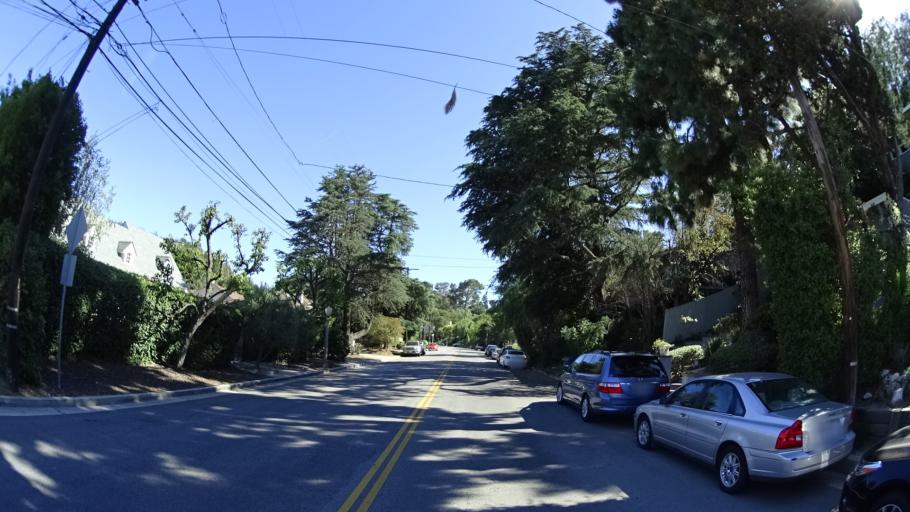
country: US
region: California
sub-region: Los Angeles County
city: Sherman Oaks
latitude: 34.1479
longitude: -118.4609
